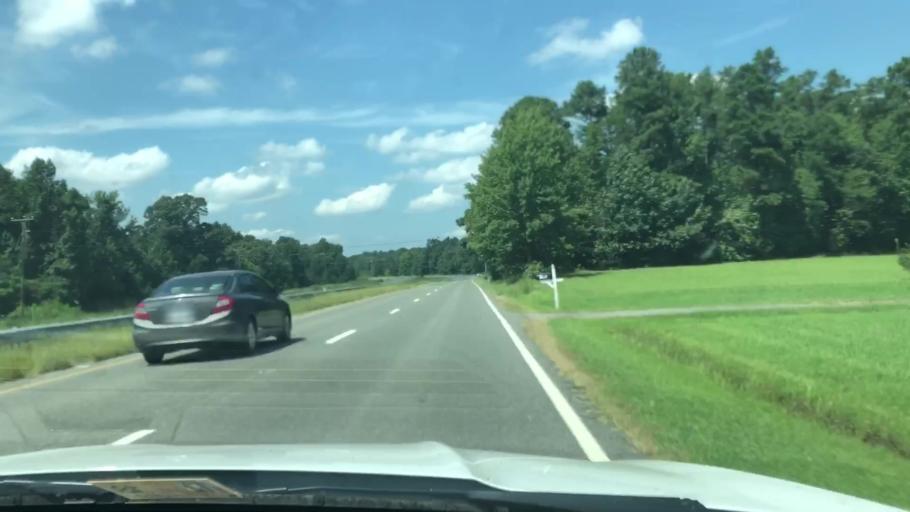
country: US
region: Virginia
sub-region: Richmond County
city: Warsaw
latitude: 37.9284
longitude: -76.7275
